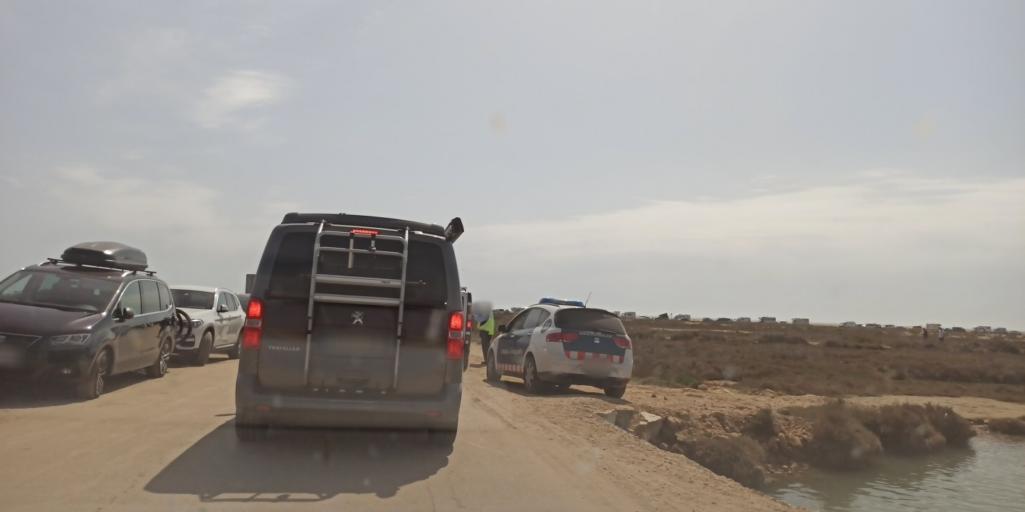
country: ES
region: Catalonia
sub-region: Provincia de Tarragona
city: Deltebre
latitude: 40.6368
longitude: 0.7458
